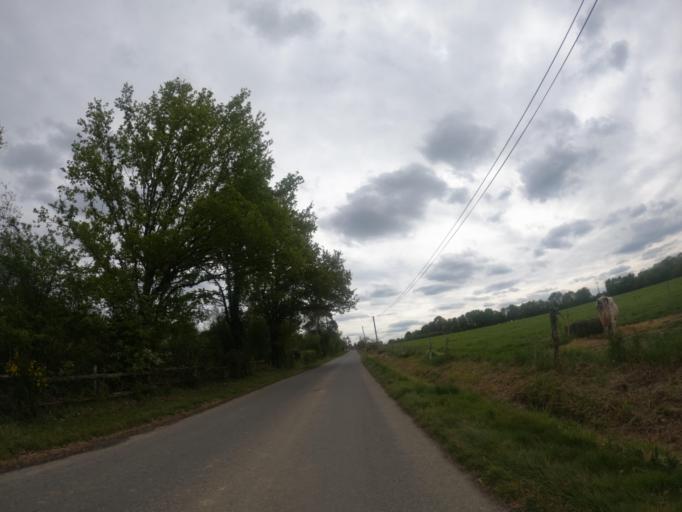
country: FR
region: Pays de la Loire
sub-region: Departement de la Loire-Atlantique
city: Chateaubriant
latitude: 47.7349
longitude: -1.4305
